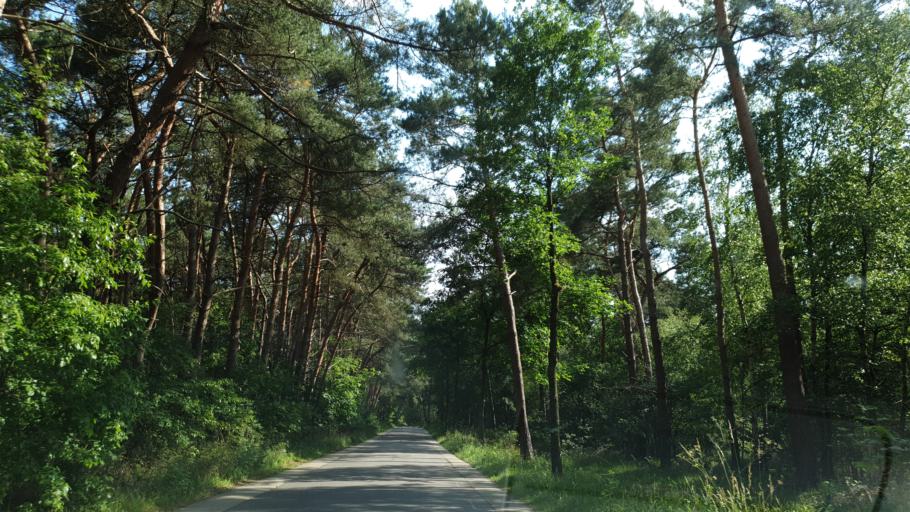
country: NL
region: Limburg
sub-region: Gemeente Weert
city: Weert
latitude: 51.2645
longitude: 5.6447
